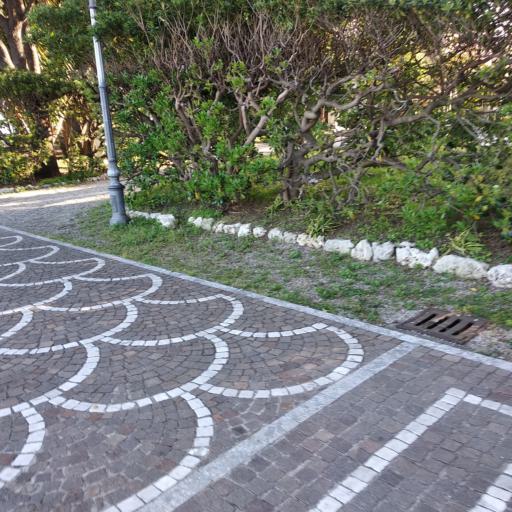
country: IT
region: Calabria
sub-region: Provincia di Reggio Calabria
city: Seminara
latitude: 38.3567
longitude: 15.8442
